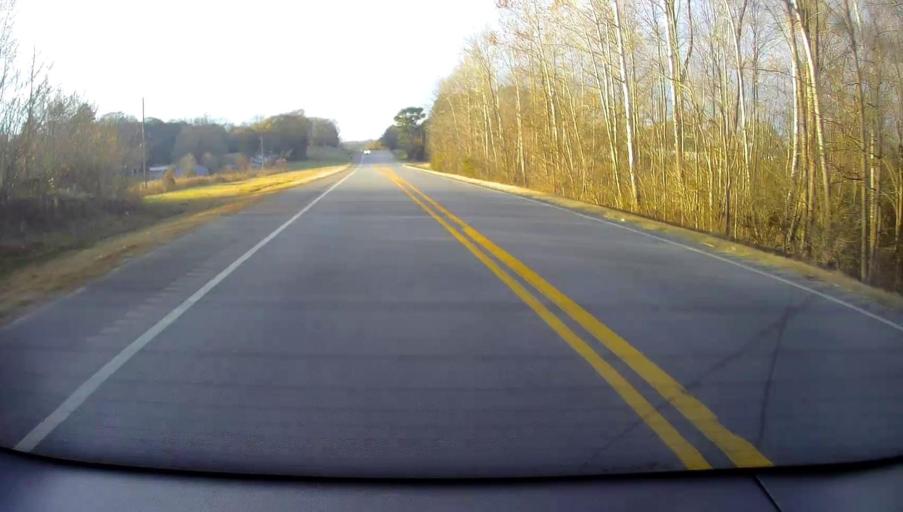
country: US
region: Alabama
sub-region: Blount County
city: Blountsville
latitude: 34.1579
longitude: -86.4649
